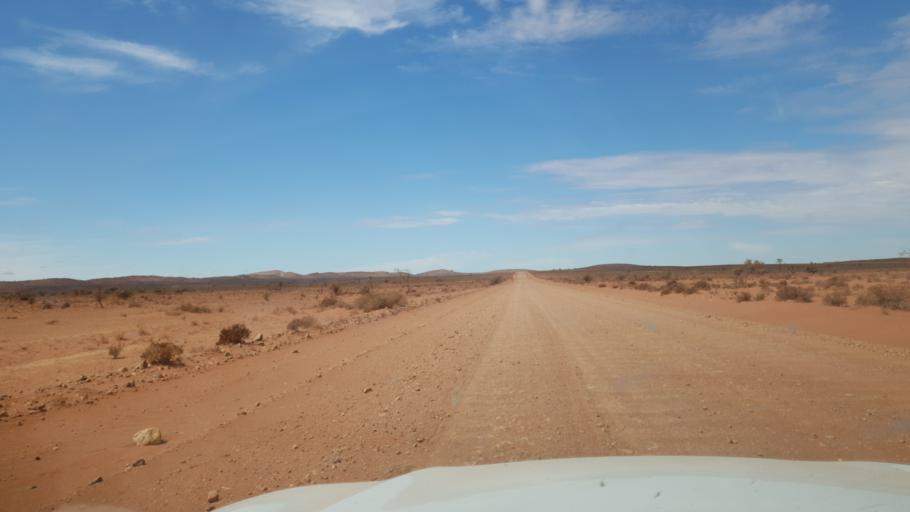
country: AU
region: South Australia
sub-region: Peterborough
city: Peterborough
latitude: -32.2162
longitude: 139.3820
